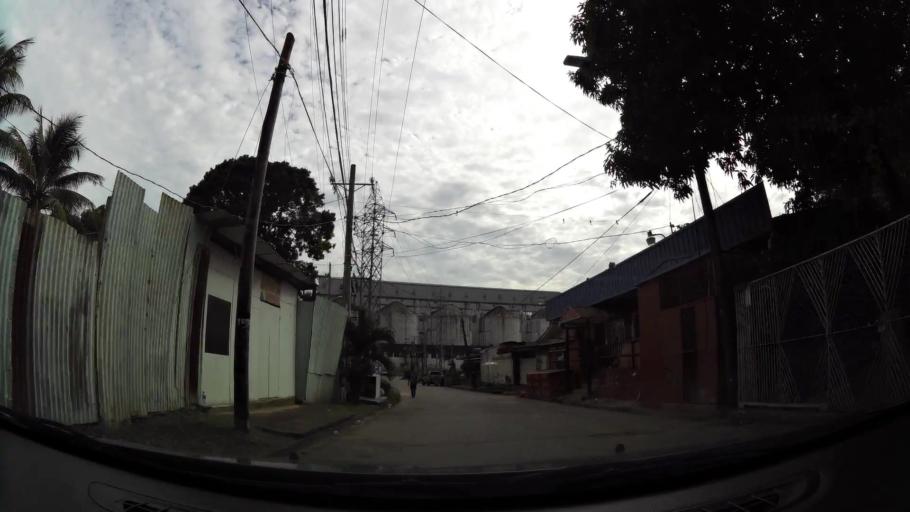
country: TT
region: City of Port of Spain
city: Mucurapo
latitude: 10.6863
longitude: -61.5963
